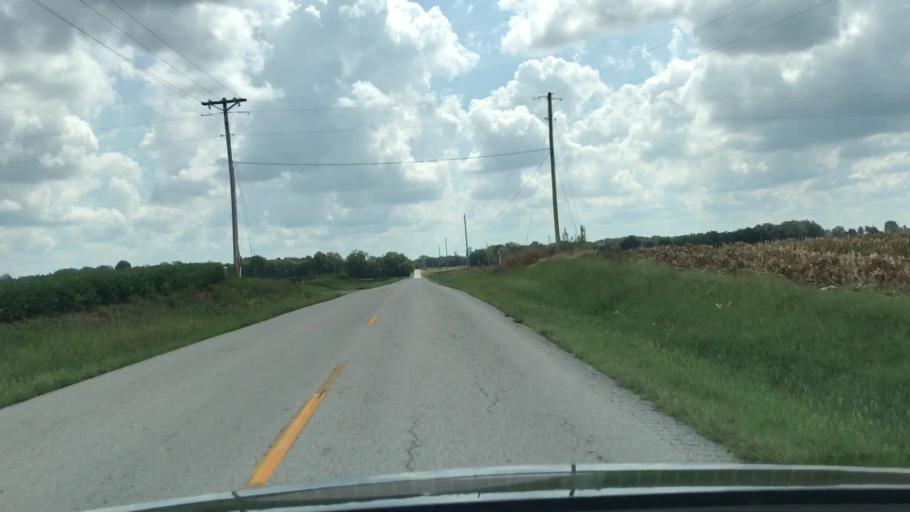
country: US
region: Kentucky
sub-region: Todd County
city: Elkton
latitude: 36.7697
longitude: -87.1146
